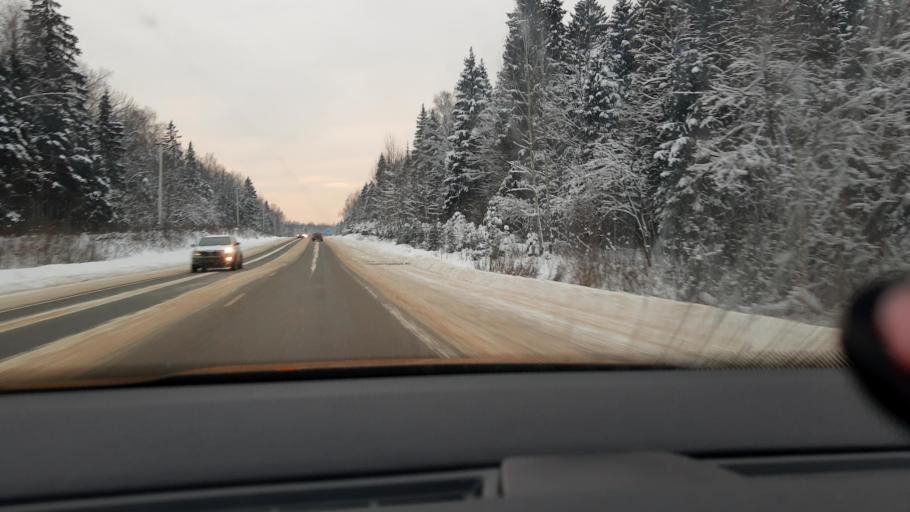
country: RU
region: Moskovskaya
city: Yershovo
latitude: 55.7992
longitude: 36.9324
